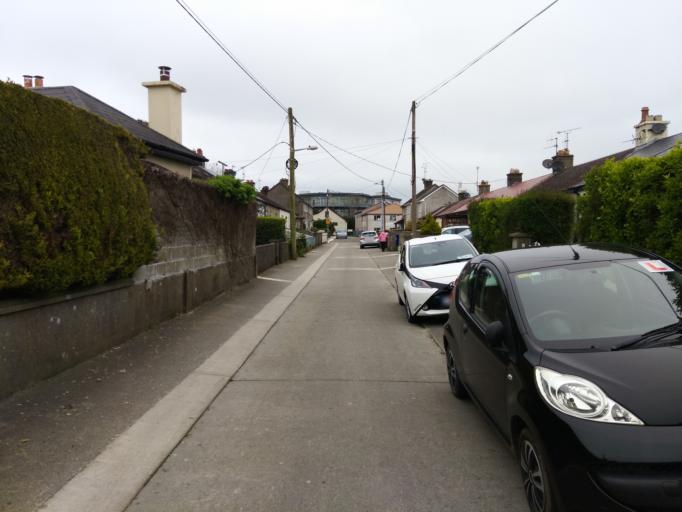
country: IE
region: Leinster
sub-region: Loch Garman
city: Loch Garman
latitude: 52.3385
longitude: -6.4690
